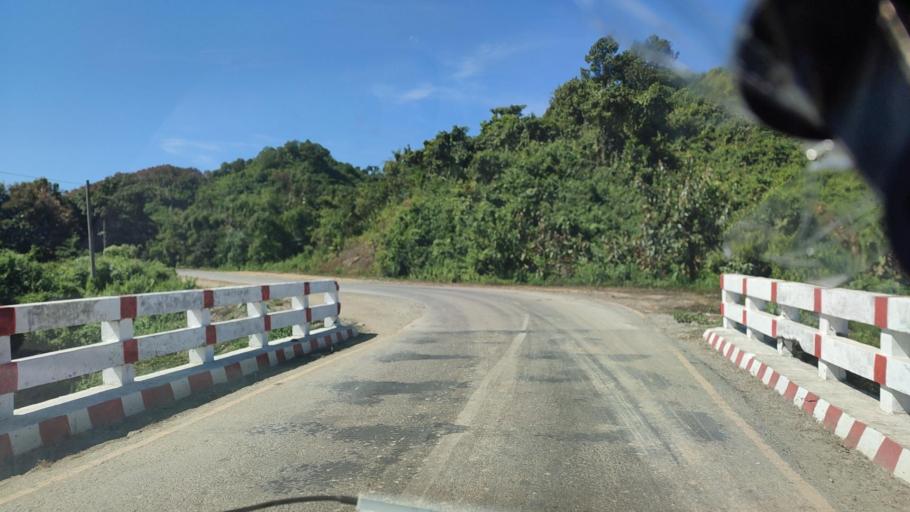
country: MM
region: Rakhine
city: Sittwe
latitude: 20.1308
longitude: 93.4617
